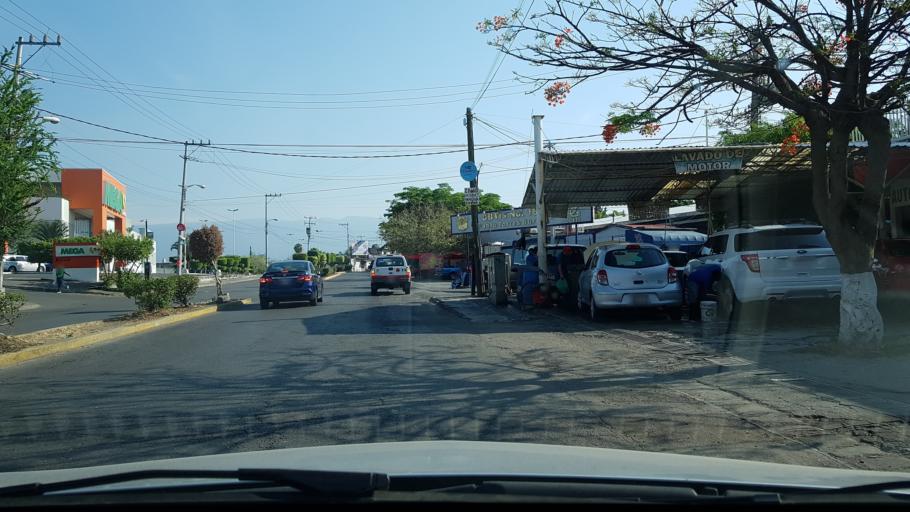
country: MX
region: Morelos
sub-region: Jiutepec
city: Jiutepec
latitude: 18.8958
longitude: -99.1667
